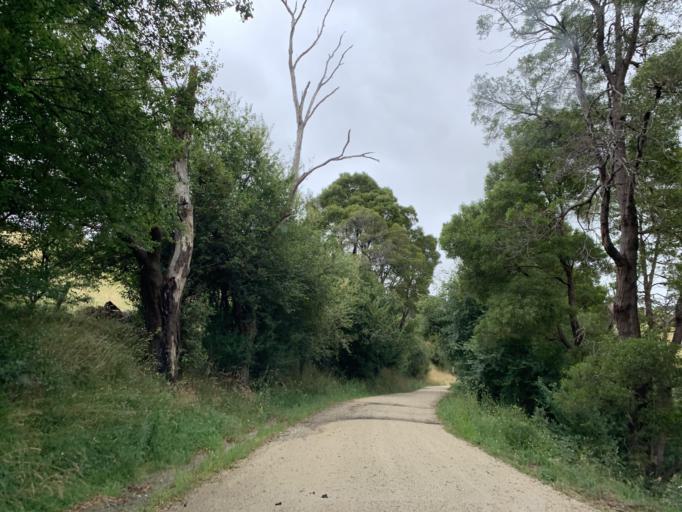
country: AU
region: Victoria
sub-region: Baw Baw
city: Warragul
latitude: -38.3303
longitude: 145.8664
